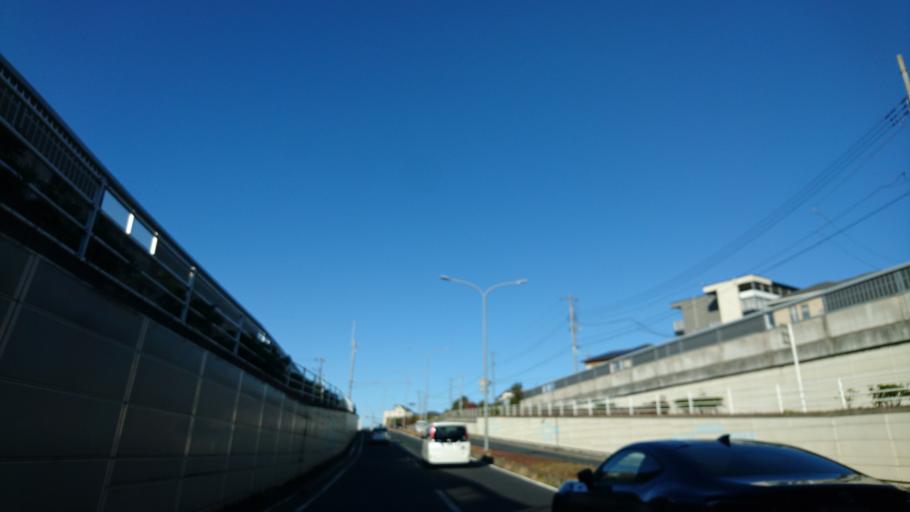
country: JP
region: Chiba
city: Chiba
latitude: 35.5701
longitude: 140.1340
